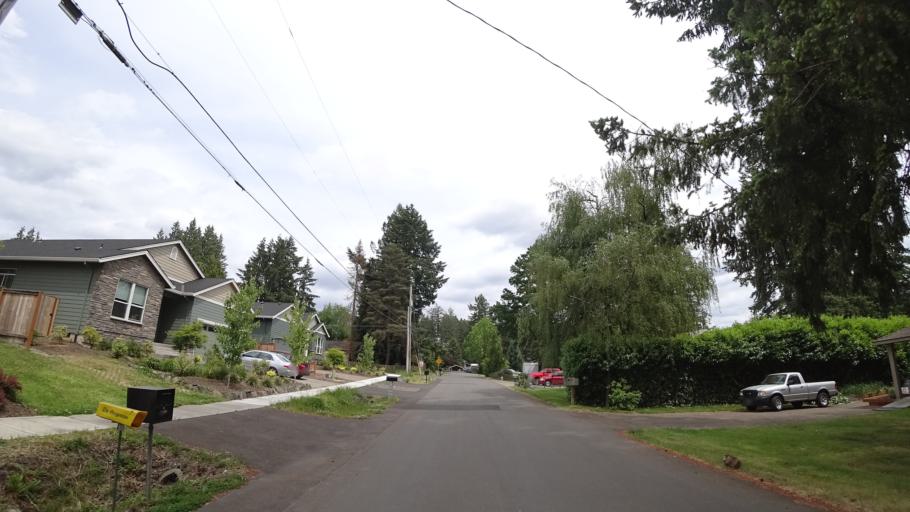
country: US
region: Oregon
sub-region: Washington County
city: Metzger
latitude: 45.4516
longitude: -122.7573
